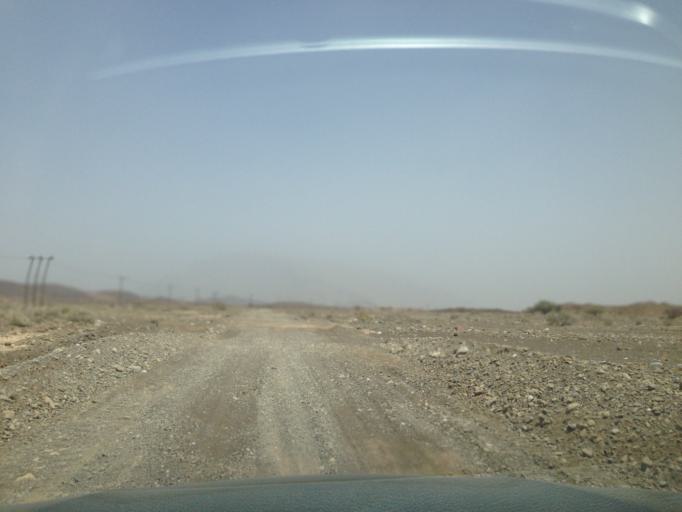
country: OM
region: Az Zahirah
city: `Ibri
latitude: 23.2391
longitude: 56.8022
